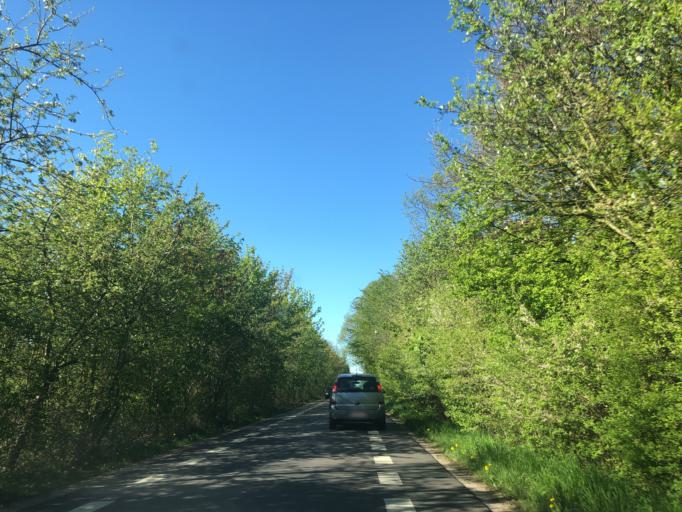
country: DK
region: Zealand
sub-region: Koge Kommune
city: Koge
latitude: 55.4258
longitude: 12.1424
